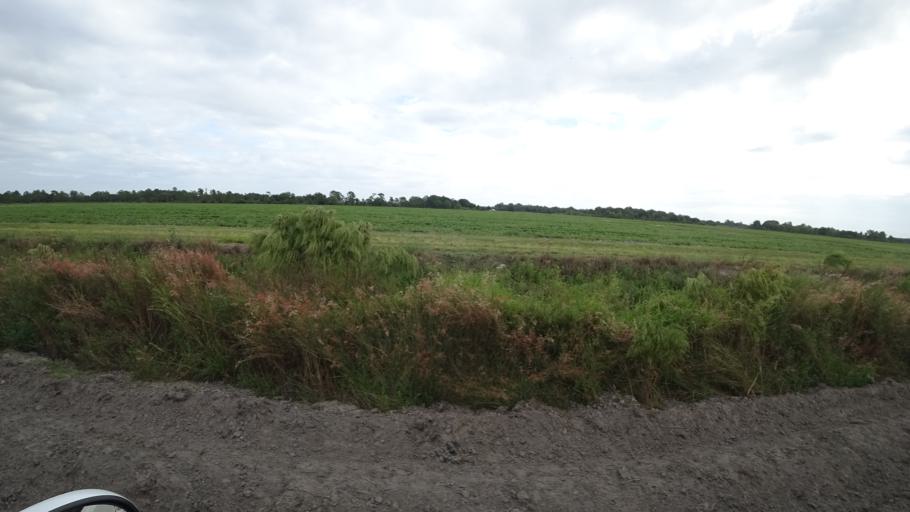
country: US
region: Florida
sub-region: Hillsborough County
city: Wimauma
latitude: 27.5654
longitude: -82.2945
